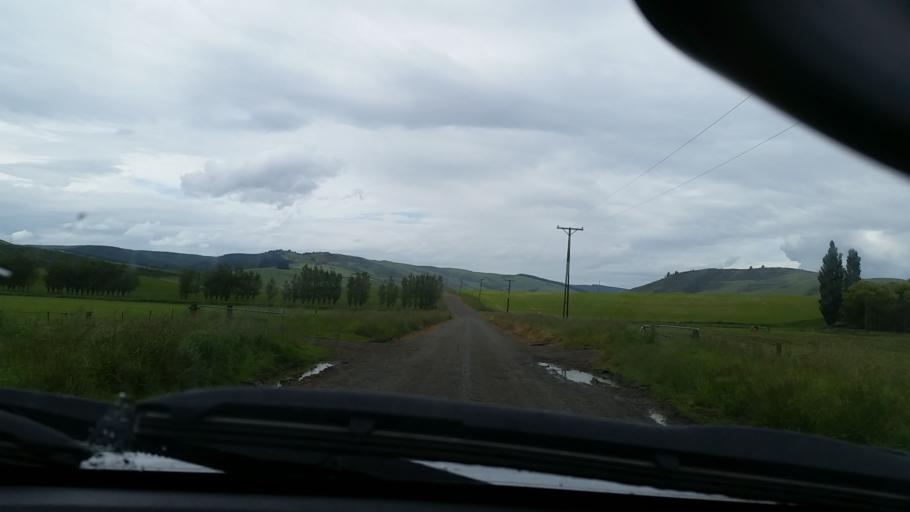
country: NZ
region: Southland
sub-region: Southland District
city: Winton
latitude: -45.9469
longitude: 168.1344
